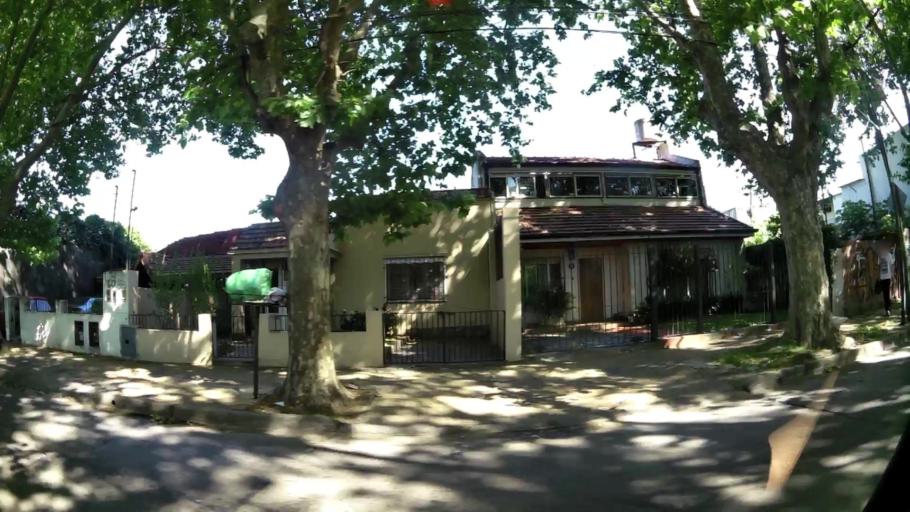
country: AR
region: Buenos Aires
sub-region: Partido de San Isidro
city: San Isidro
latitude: -34.4679
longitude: -58.5278
